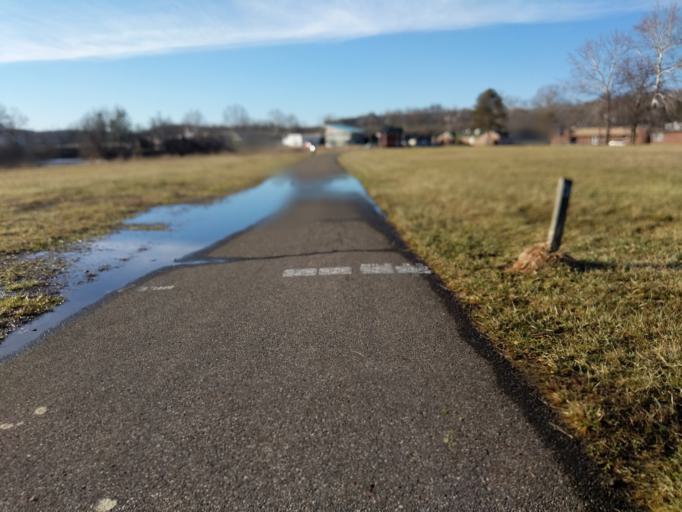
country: US
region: Ohio
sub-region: Athens County
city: Athens
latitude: 39.3299
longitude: -82.1220
